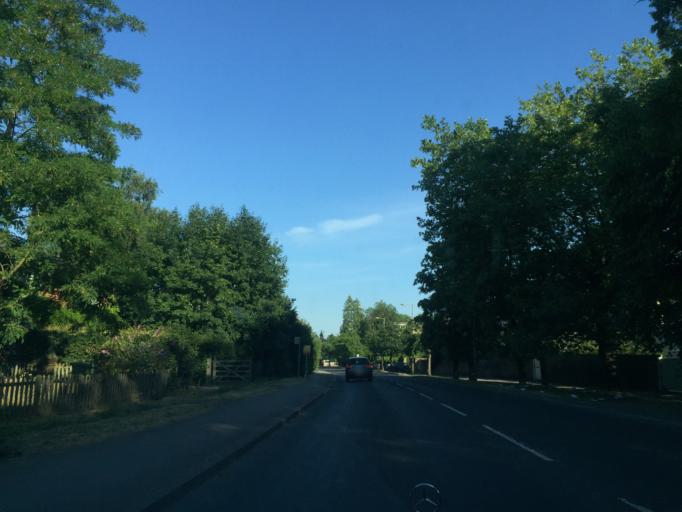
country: GB
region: England
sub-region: Oxfordshire
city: Henley on Thames
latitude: 51.5452
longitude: -0.9125
